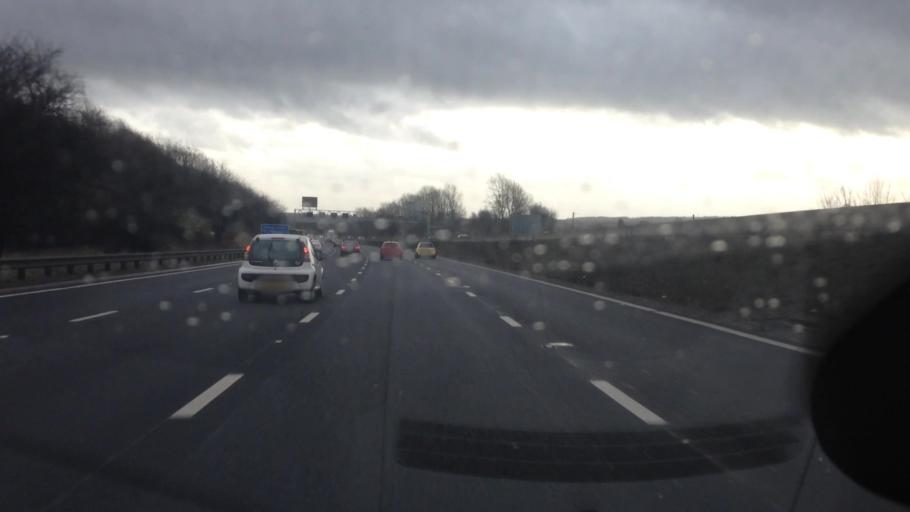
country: GB
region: England
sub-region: City and Borough of Wakefield
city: Horbury
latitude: 53.6734
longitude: -1.5503
